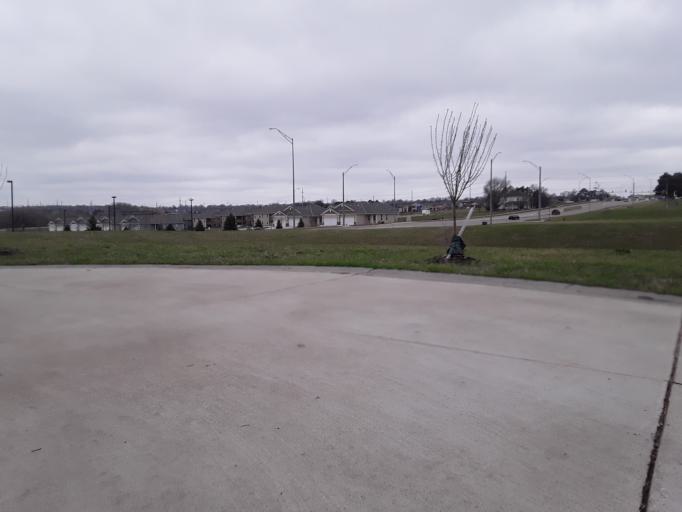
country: US
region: Nebraska
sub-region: Lancaster County
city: Lincoln
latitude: 40.8431
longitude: -96.6009
